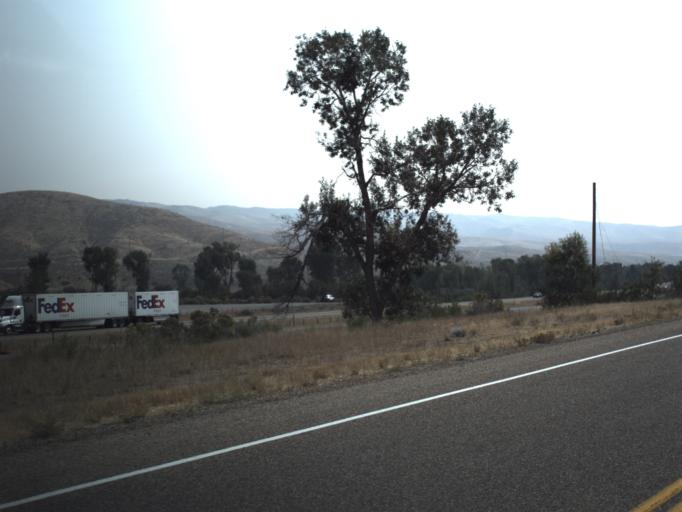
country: US
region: Utah
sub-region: Morgan County
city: Morgan
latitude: 41.0412
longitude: -111.5199
